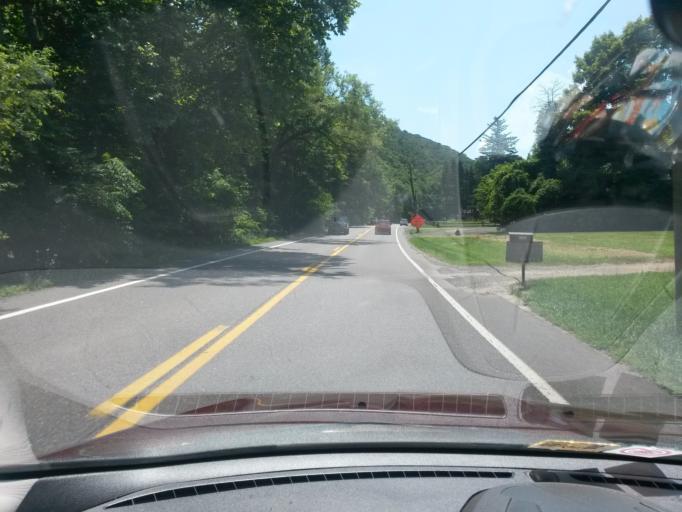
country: US
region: West Virginia
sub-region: Mineral County
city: Keyser
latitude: 39.3802
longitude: -79.0236
